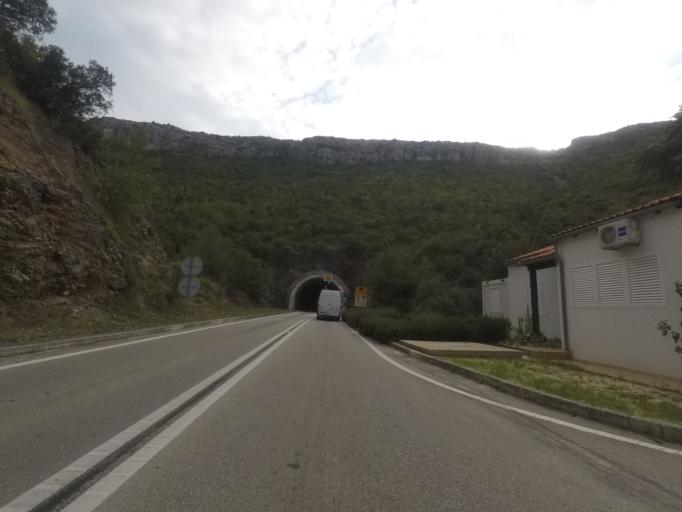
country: HR
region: Splitsko-Dalmatinska
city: Stari Grad
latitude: 43.1658
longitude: 16.5568
